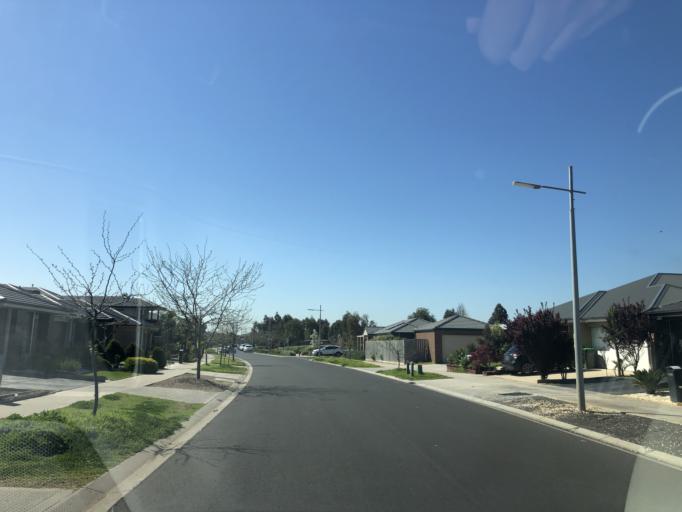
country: AU
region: Victoria
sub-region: Wyndham
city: Hoppers Crossing
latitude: -37.9000
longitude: 144.7191
